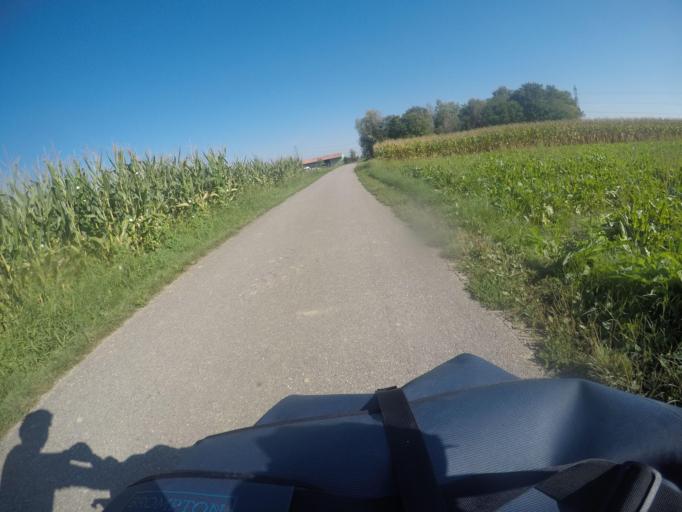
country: FR
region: Alsace
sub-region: Departement du Haut-Rhin
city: Ottmarsheim
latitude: 47.7674
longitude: 7.5051
